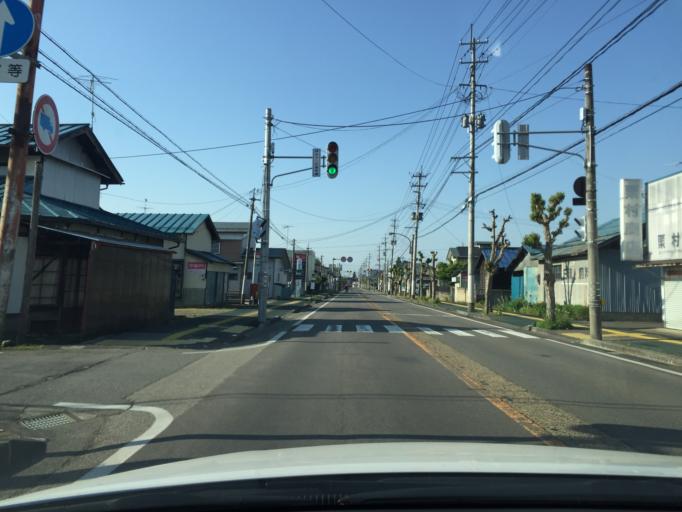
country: JP
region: Fukushima
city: Kitakata
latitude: 37.6623
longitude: 139.8718
